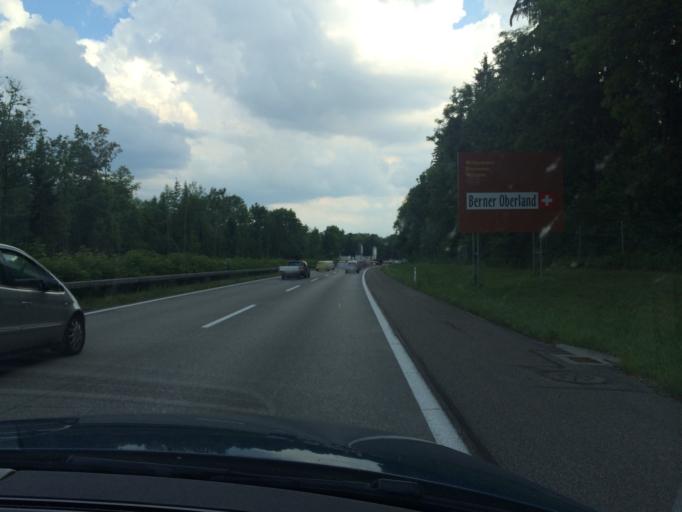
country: CH
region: Bern
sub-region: Bern-Mittelland District
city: Niederwichtrach
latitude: 46.8243
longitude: 7.5701
